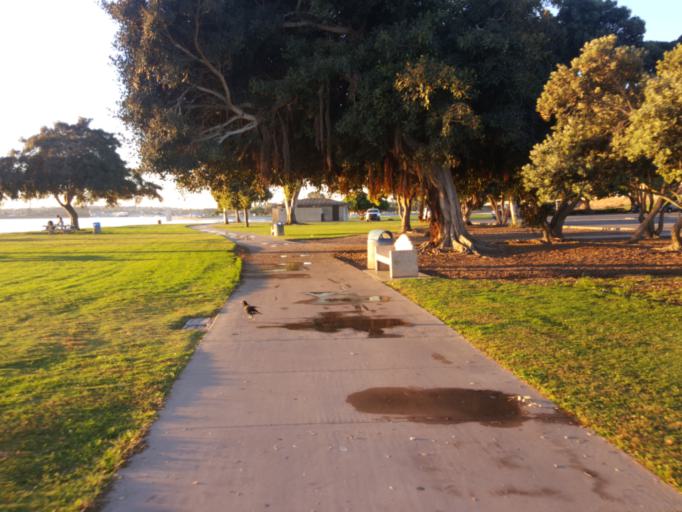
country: US
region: California
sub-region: San Diego County
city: La Jolla
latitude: 32.7839
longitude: -117.2329
